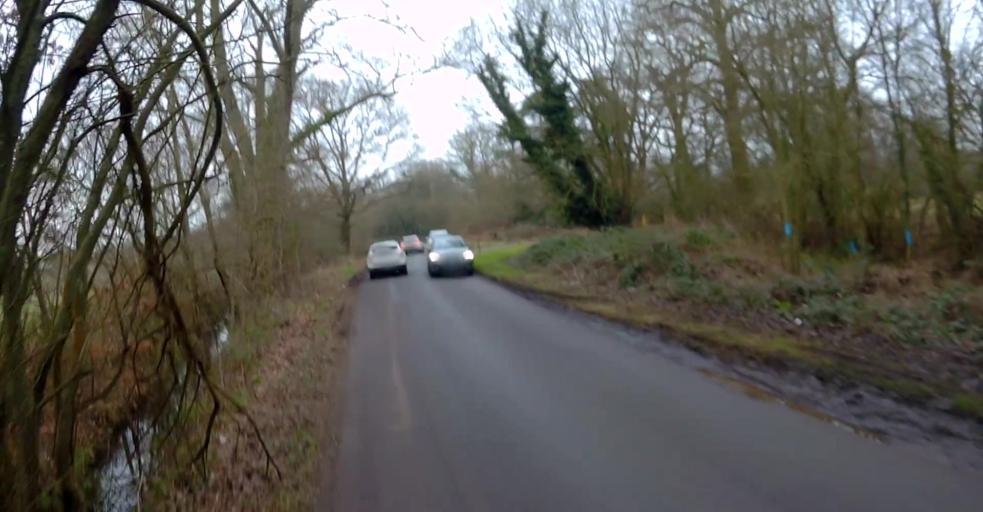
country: GB
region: England
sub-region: Hampshire
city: Eversley
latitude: 51.3683
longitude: -0.8866
